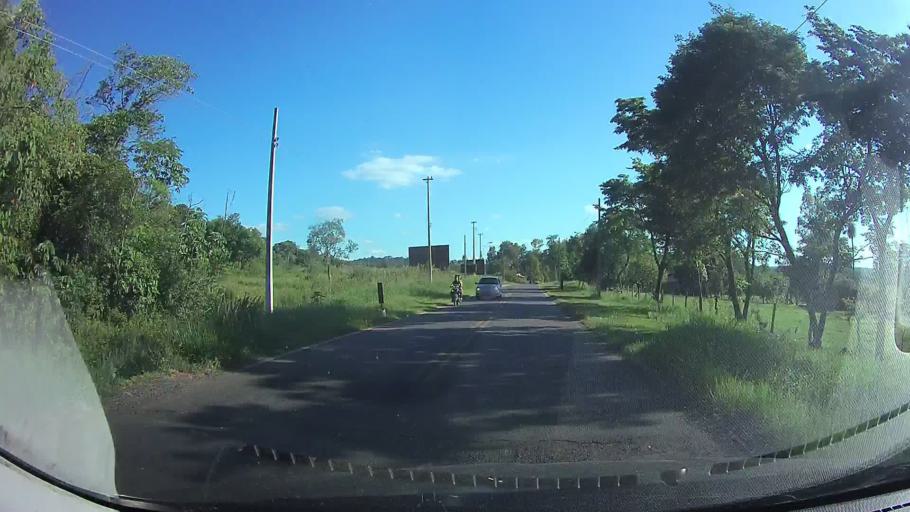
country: PY
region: Cordillera
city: Atyra
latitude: -25.2983
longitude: -57.1850
